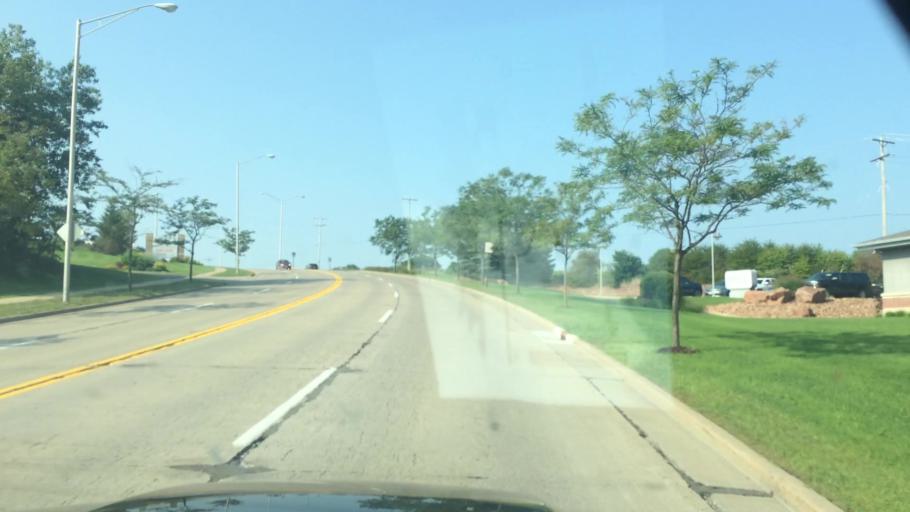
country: US
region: Wisconsin
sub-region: Marathon County
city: Wausau
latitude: 44.9688
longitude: -89.6540
